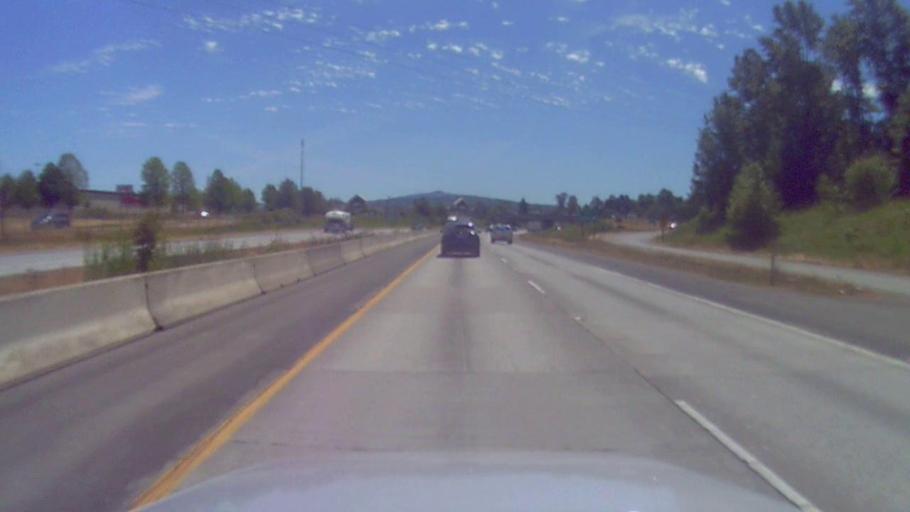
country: US
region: Washington
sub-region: Whatcom County
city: Bellingham
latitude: 48.7728
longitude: -122.4649
